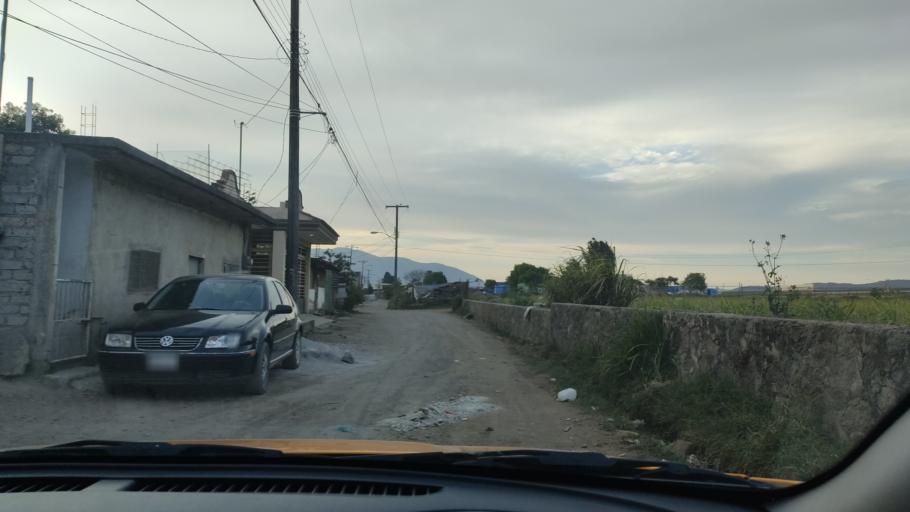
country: MX
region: Nayarit
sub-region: Tepic
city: La Corregidora
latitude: 21.4609
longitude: -104.8254
